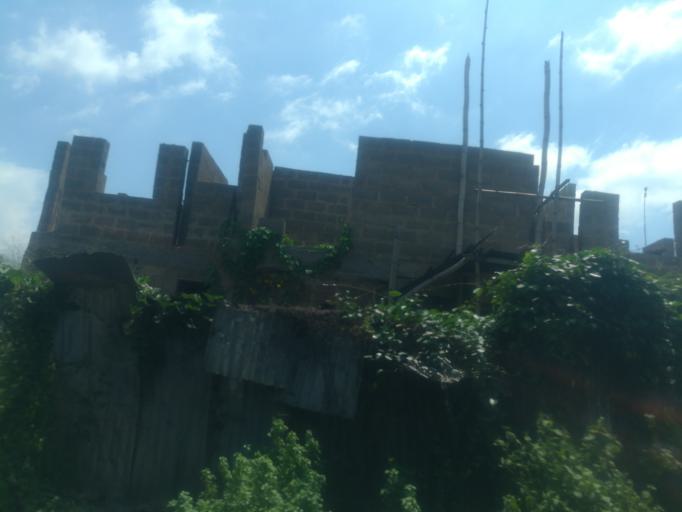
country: NG
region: Oyo
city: Ibadan
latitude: 7.3610
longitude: 3.8714
